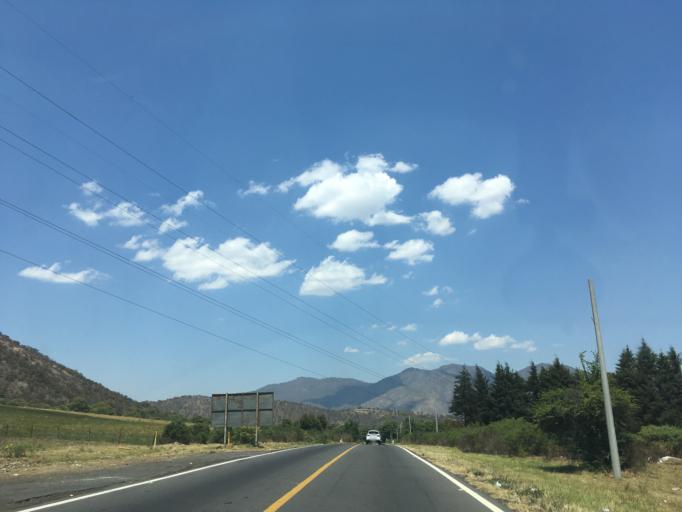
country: MX
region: Michoacan
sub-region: Chilchota
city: Tacuro (Santa Maria Tacuro)
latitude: 19.8258
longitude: -102.0284
